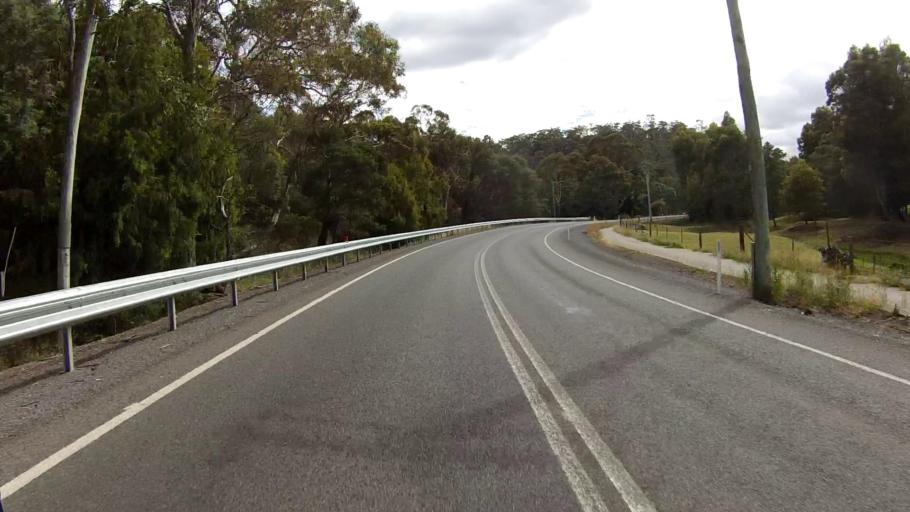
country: AU
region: Tasmania
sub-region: Glenorchy
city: Lutana
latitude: -42.8094
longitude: 147.3368
